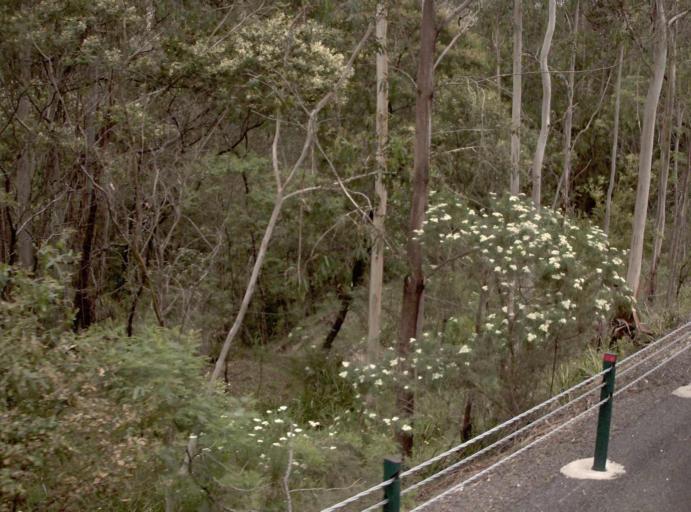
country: AU
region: New South Wales
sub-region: Bombala
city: Bombala
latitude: -37.2713
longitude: 149.2274
